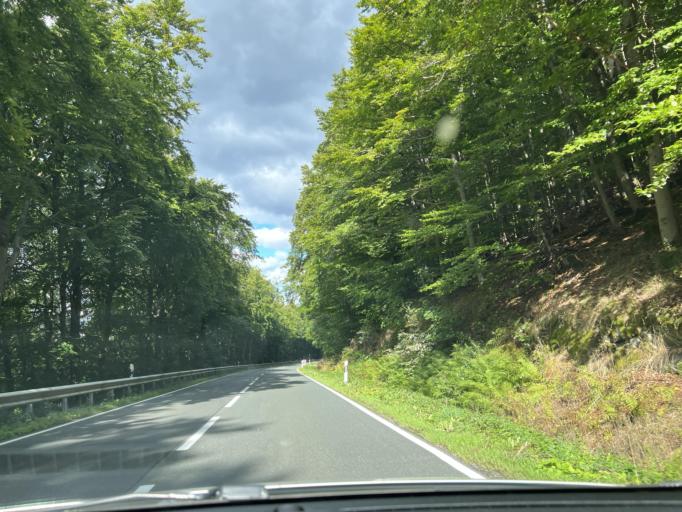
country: DE
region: North Rhine-Westphalia
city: Hilchenbach
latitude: 50.9737
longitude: 8.1415
